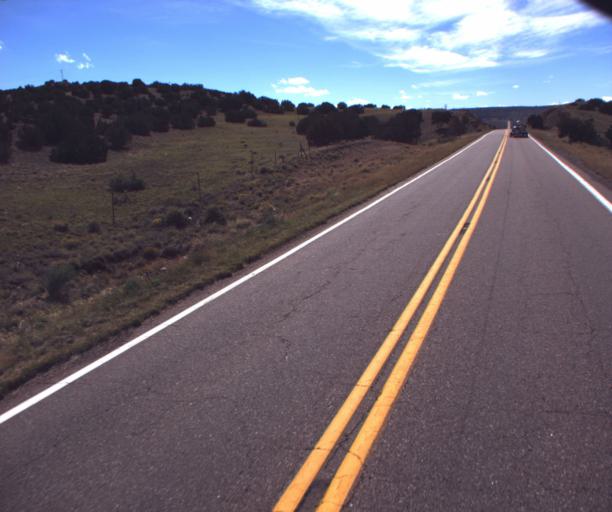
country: US
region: Arizona
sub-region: Apache County
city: Saint Johns
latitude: 34.4853
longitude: -109.5845
